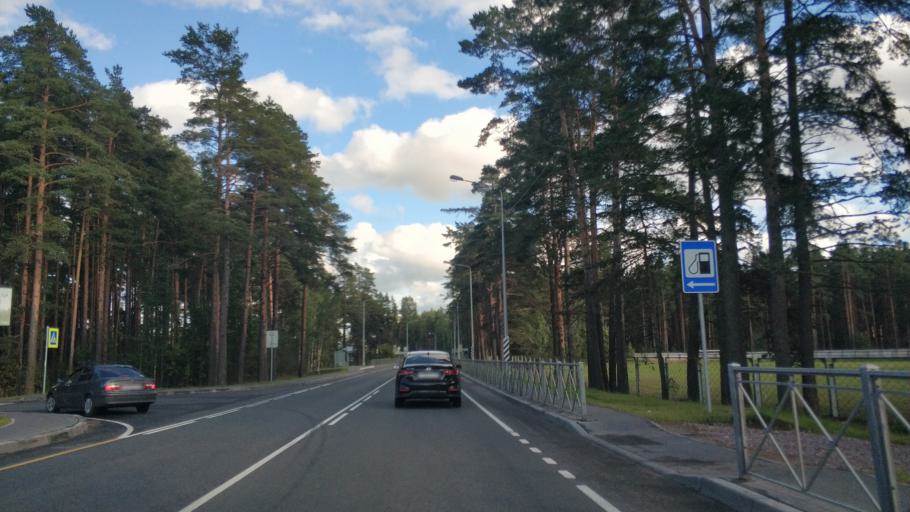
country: RU
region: Leningrad
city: Priozersk
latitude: 61.0187
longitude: 30.1360
